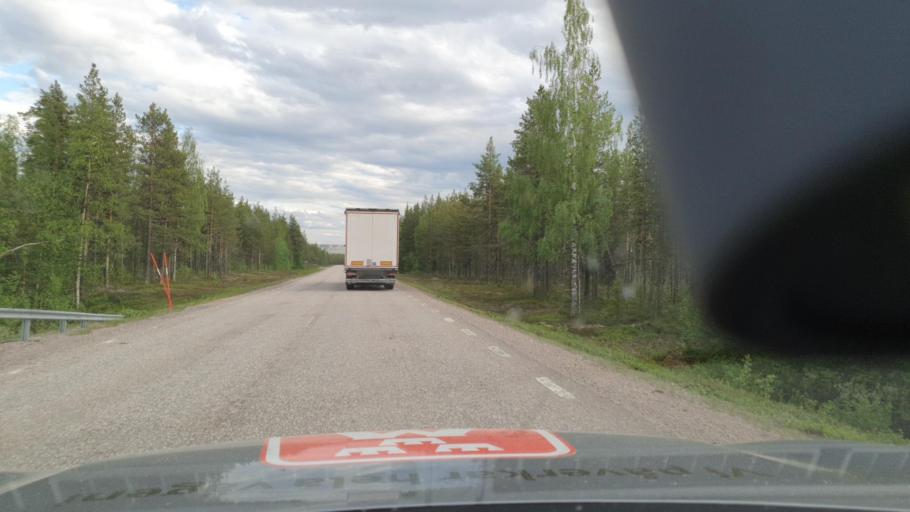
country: SE
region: Norrbotten
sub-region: Gallivare Kommun
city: Gaellivare
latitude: 67.1266
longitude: 20.9014
